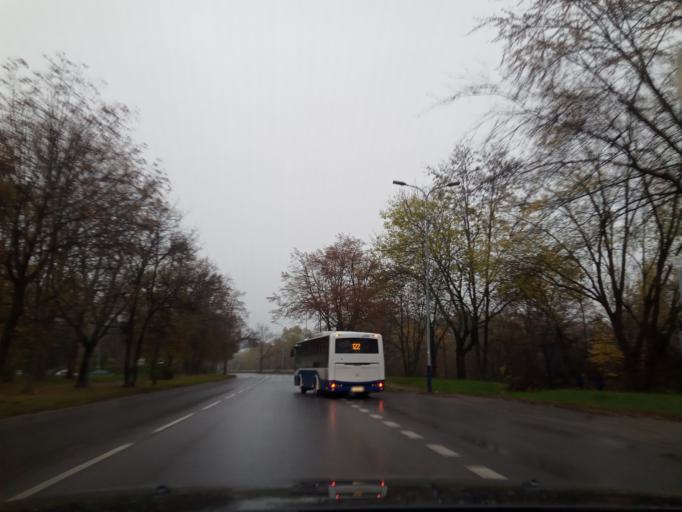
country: PL
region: Lesser Poland Voivodeship
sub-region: Powiat wielicki
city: Kokotow
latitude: 50.0917
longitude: 20.0597
